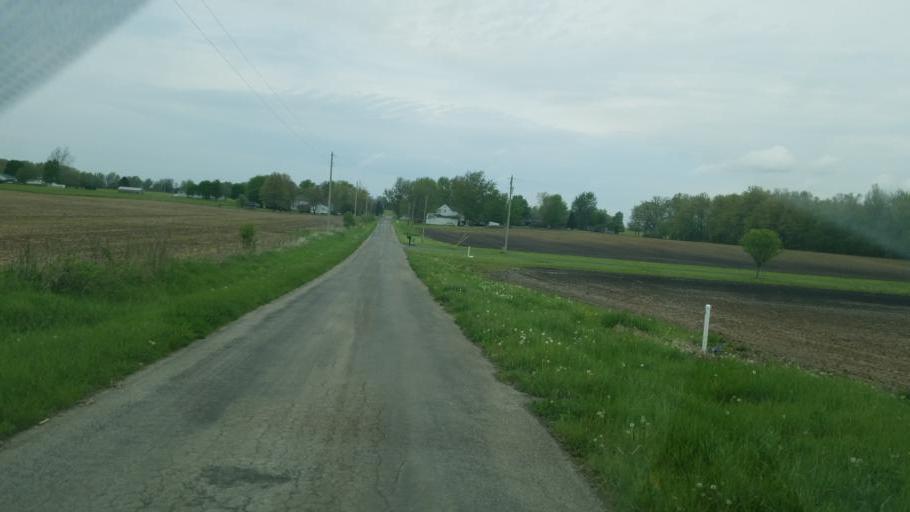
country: US
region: Ohio
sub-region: Huron County
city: Willard
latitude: 41.0280
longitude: -82.7403
